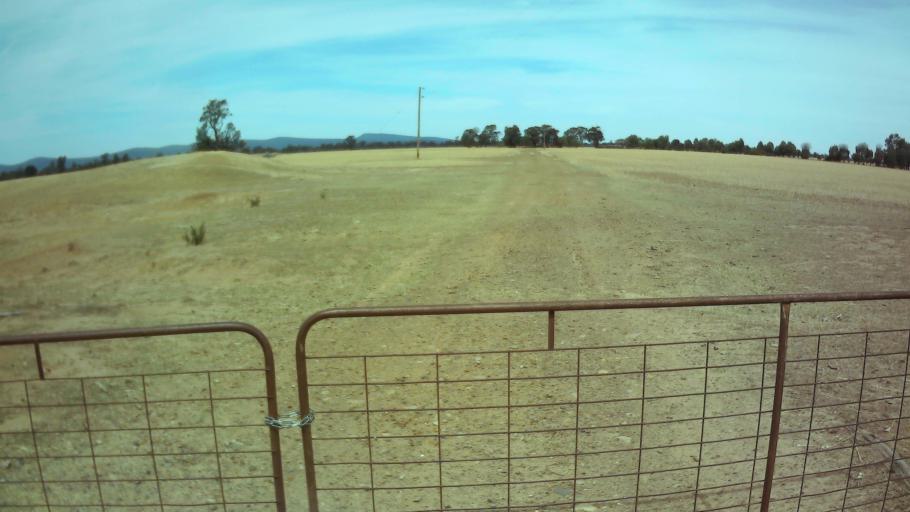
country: AU
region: New South Wales
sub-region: Weddin
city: Grenfell
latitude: -33.9433
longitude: 147.7930
